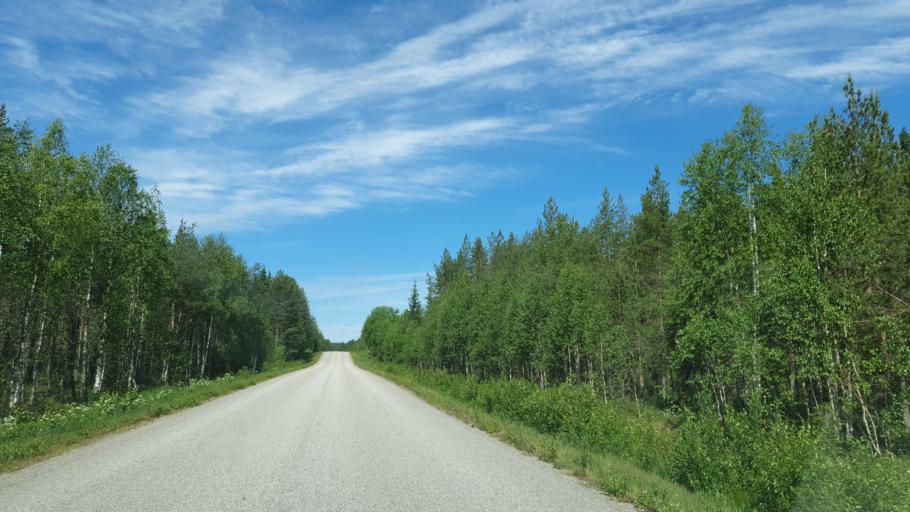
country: FI
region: Kainuu
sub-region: Kehys-Kainuu
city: Suomussalmi
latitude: 64.5872
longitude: 29.1129
